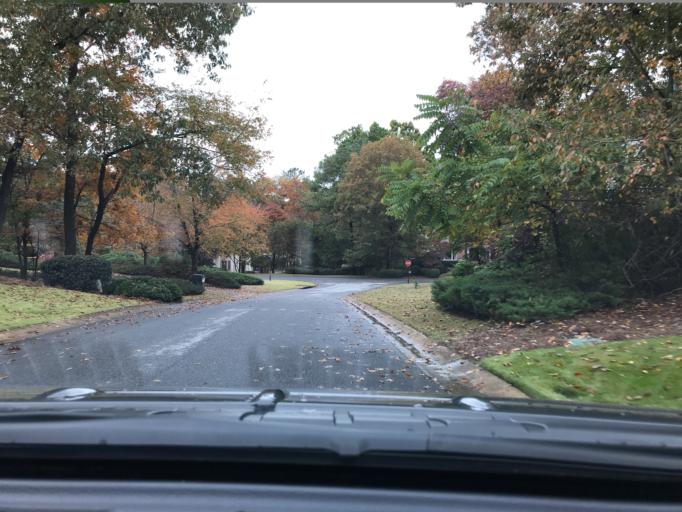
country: US
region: Georgia
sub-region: Fulton County
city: Johns Creek
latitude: 34.0061
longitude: -84.2314
